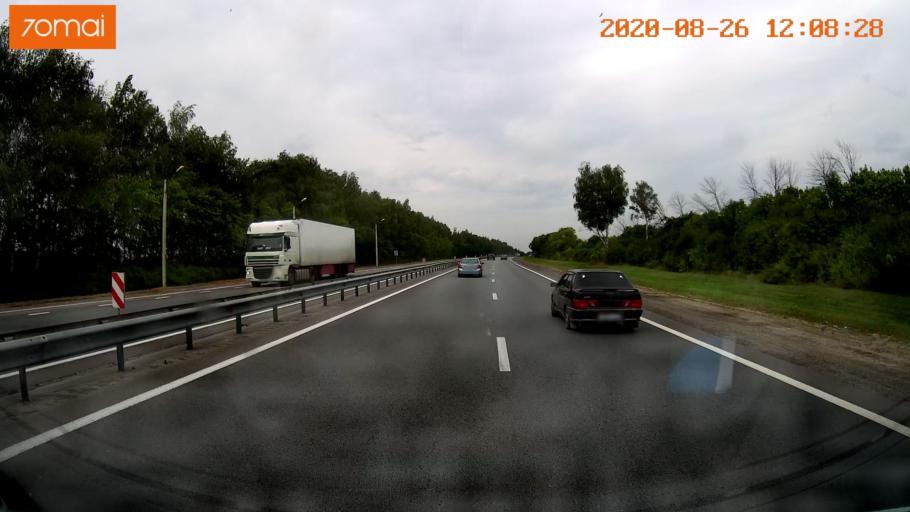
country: RU
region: Rjazan
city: Starozhilovo
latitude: 54.3517
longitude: 40.1190
